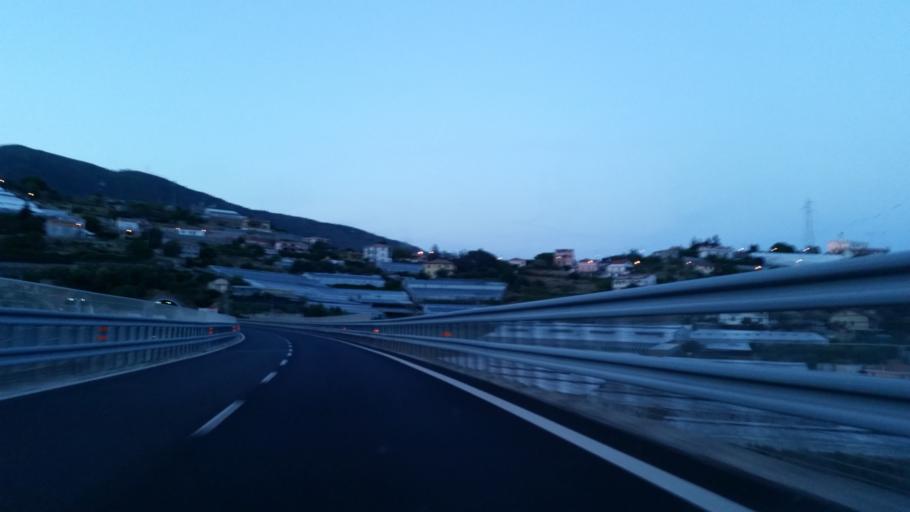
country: IT
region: Liguria
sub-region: Provincia di Imperia
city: San Remo
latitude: 43.8260
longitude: 7.7443
